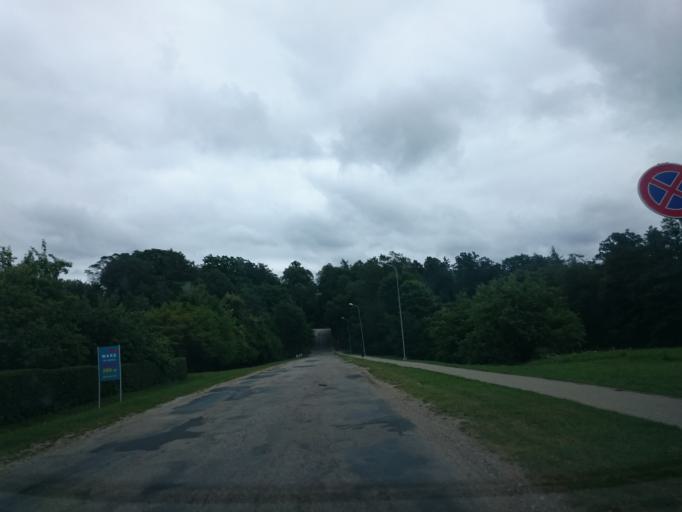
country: LV
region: Pavilostas
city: Pavilosta
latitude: 56.8813
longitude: 21.2085
